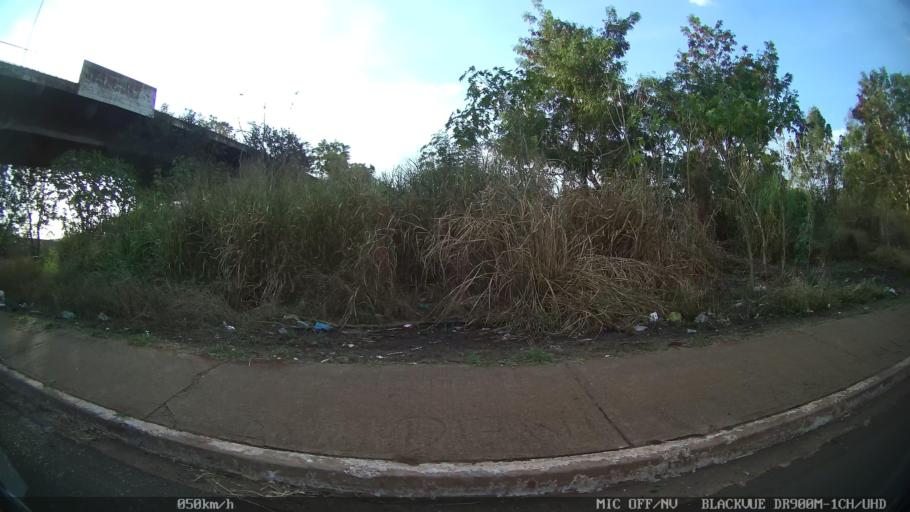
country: BR
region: Sao Paulo
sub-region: Ribeirao Preto
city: Ribeirao Preto
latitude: -21.1373
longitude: -47.8027
